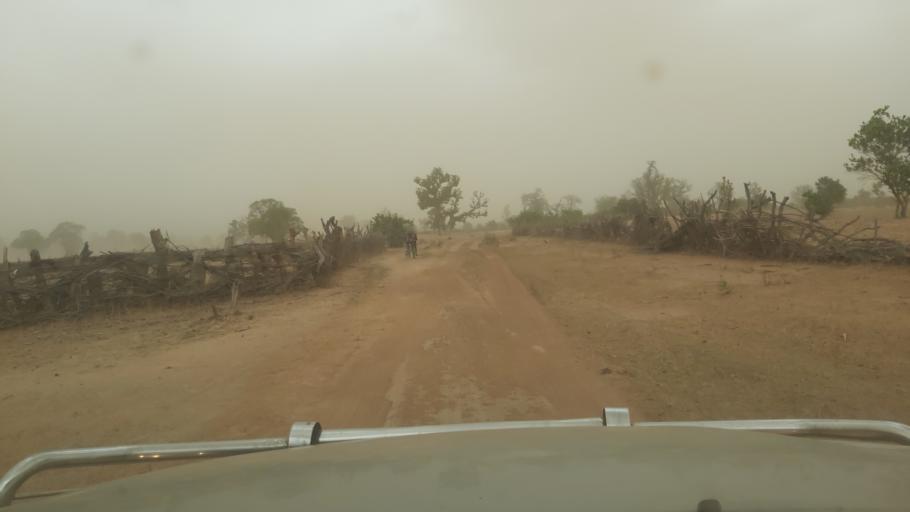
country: ML
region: Koulikoro
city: Banamba
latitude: 13.3783
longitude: -7.2053
